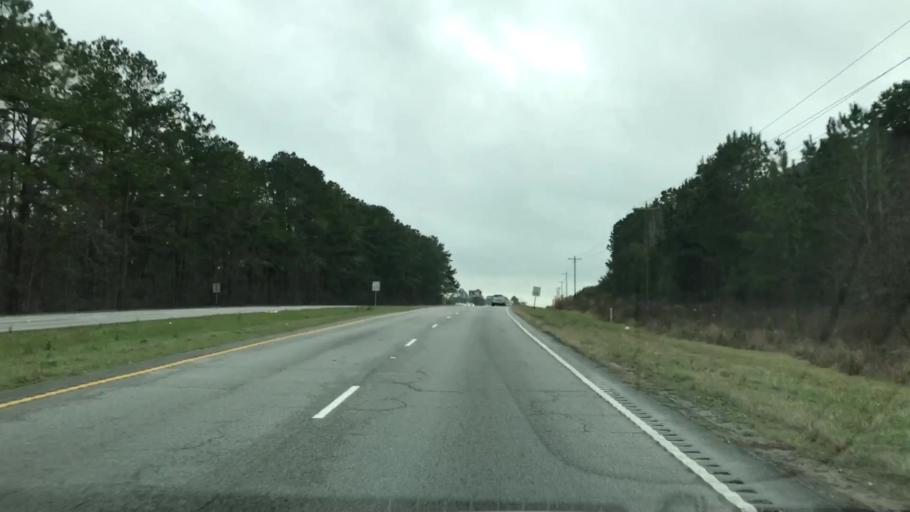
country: US
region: South Carolina
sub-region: Berkeley County
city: Goose Creek
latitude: 33.0437
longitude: -80.0332
